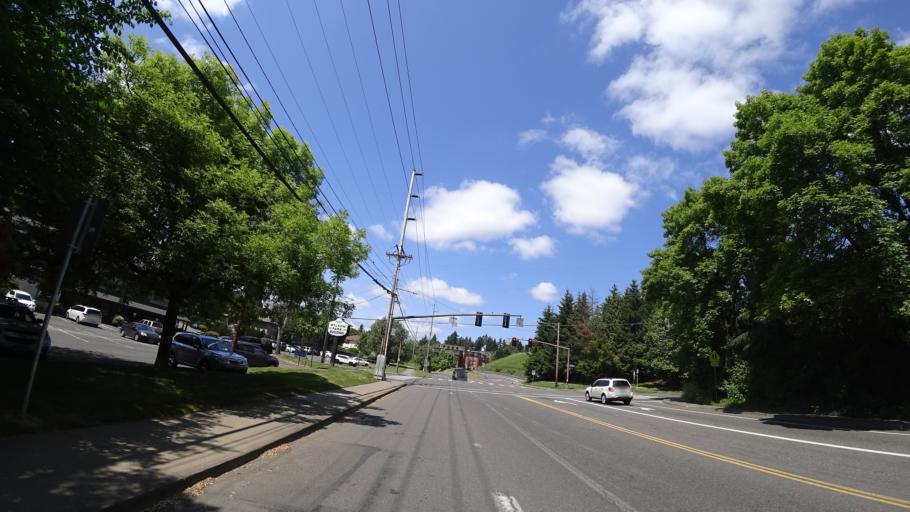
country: US
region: Oregon
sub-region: Multnomah County
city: Portland
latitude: 45.4757
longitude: -122.6964
